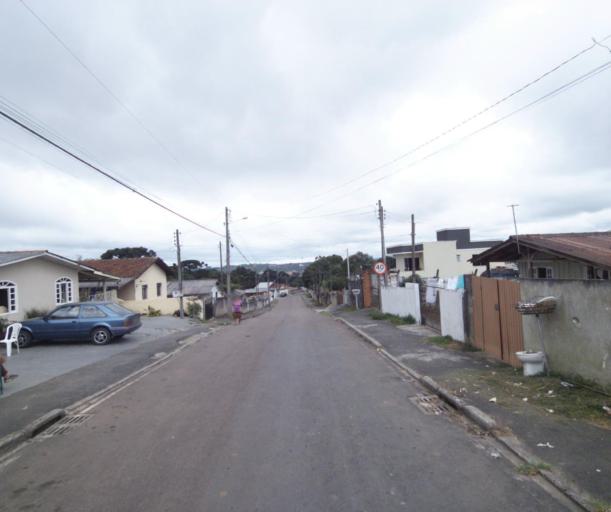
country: BR
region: Parana
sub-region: Quatro Barras
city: Quatro Barras
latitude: -25.3661
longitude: -49.1155
